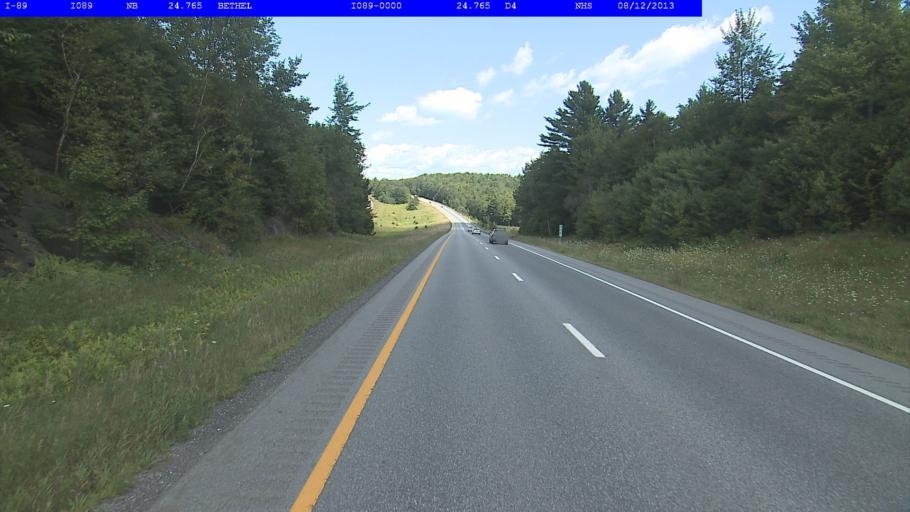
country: US
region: Vermont
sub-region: Orange County
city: Randolph
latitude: 43.8579
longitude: -72.6068
